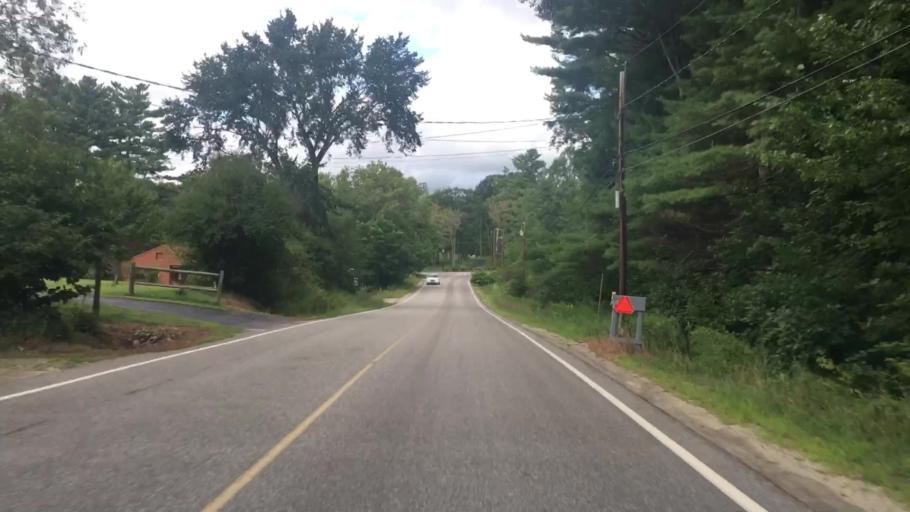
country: US
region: Maine
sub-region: York County
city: West Kennebunk
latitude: 43.4546
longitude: -70.6198
